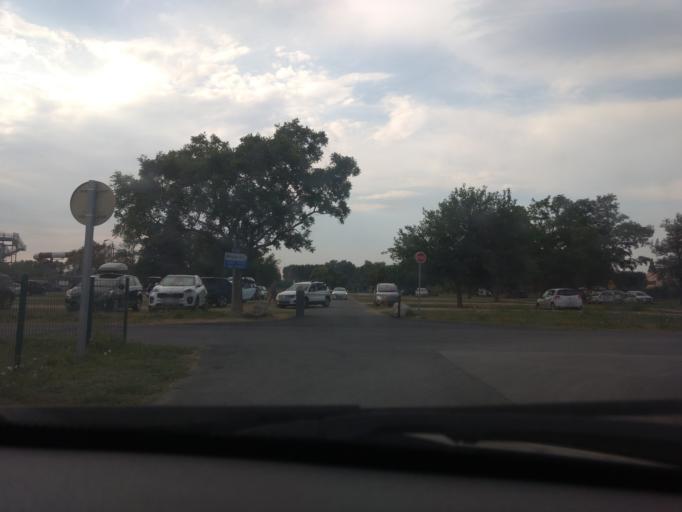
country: FR
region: Languedoc-Roussillon
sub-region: Departement des Pyrenees-Orientales
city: Latour-Bas-Elne
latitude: 42.6009
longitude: 3.0312
